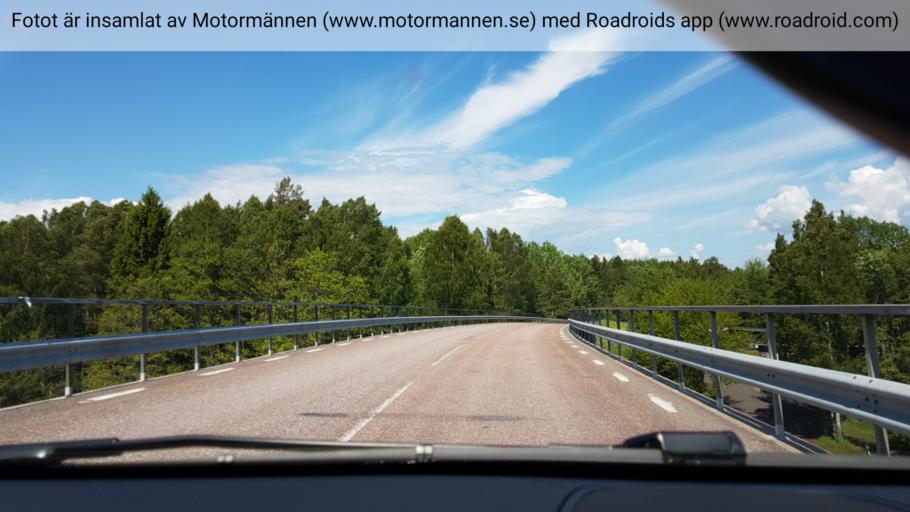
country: SE
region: Stockholm
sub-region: Nynashamns Kommun
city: Nynashamn
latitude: 58.9571
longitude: 17.9625
